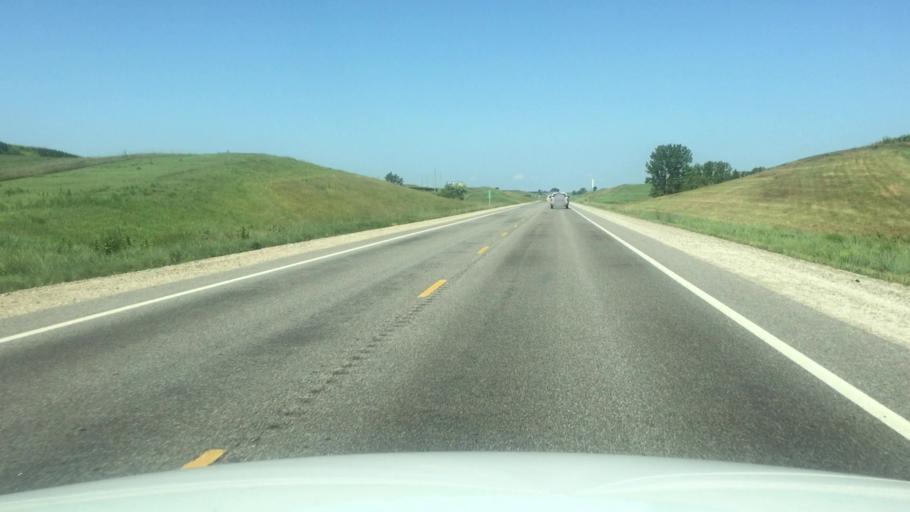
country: US
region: Kansas
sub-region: Doniphan County
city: Highland
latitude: 39.8422
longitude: -95.3111
